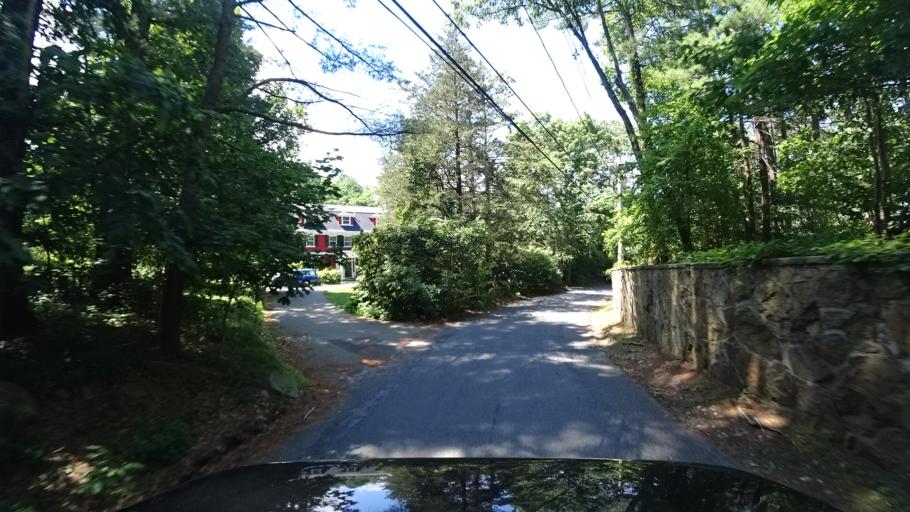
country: US
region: Massachusetts
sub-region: Norfolk County
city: Dedham
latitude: 42.2441
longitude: -71.1848
